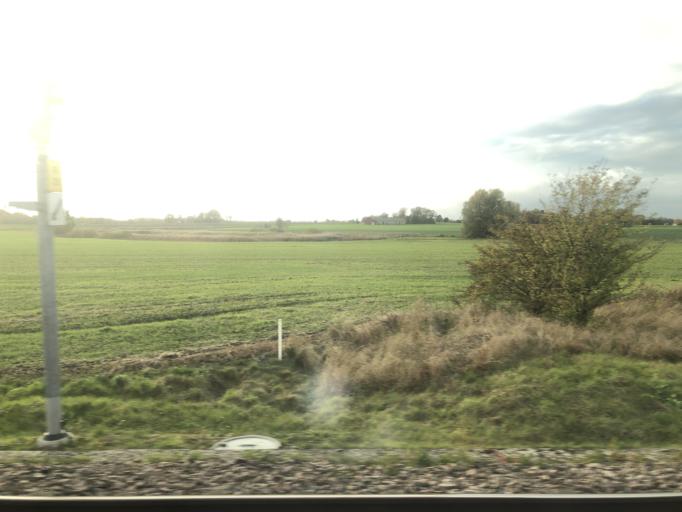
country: SE
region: Skane
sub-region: Lomma Kommun
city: Lomma
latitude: 55.7228
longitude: 13.0749
